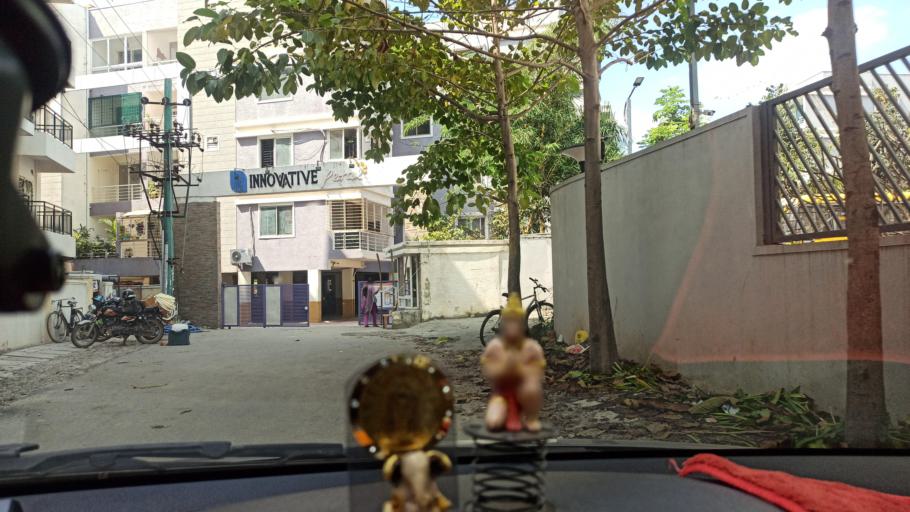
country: IN
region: Karnataka
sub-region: Bangalore Urban
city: Bangalore
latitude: 12.9777
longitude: 77.6919
